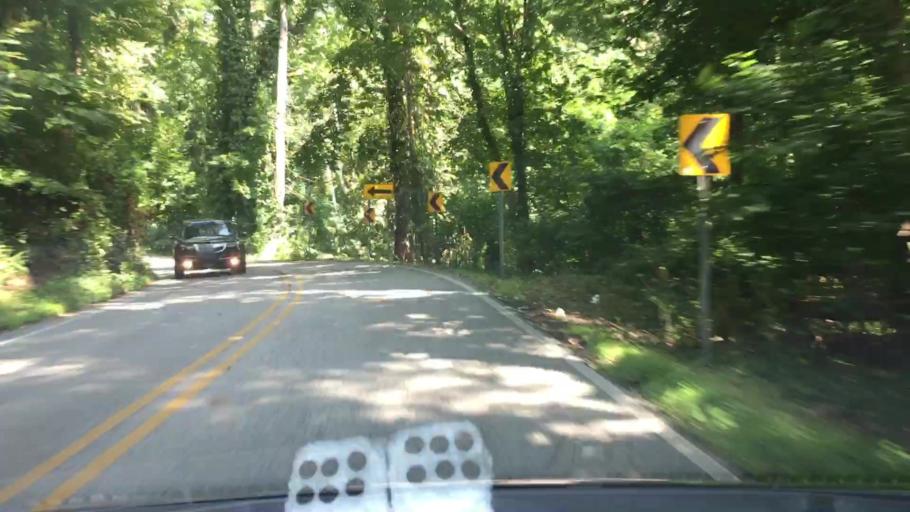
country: US
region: Pennsylvania
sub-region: Delaware County
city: Media
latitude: 39.8996
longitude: -75.3924
